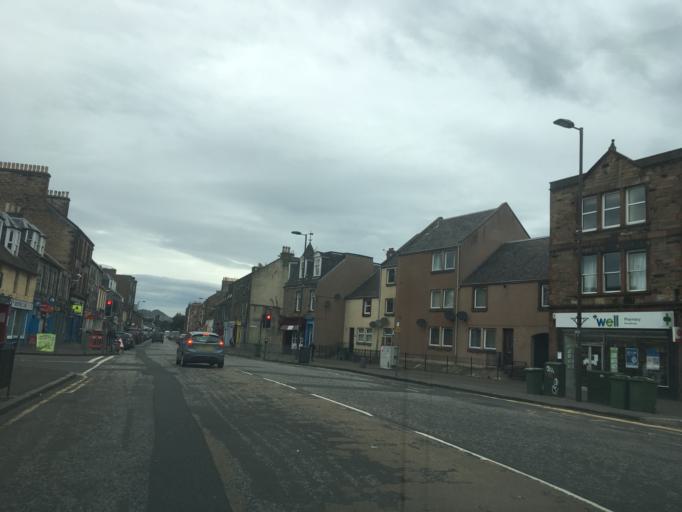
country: GB
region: Scotland
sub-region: East Lothian
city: Musselburgh
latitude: 55.9439
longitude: -3.0583
